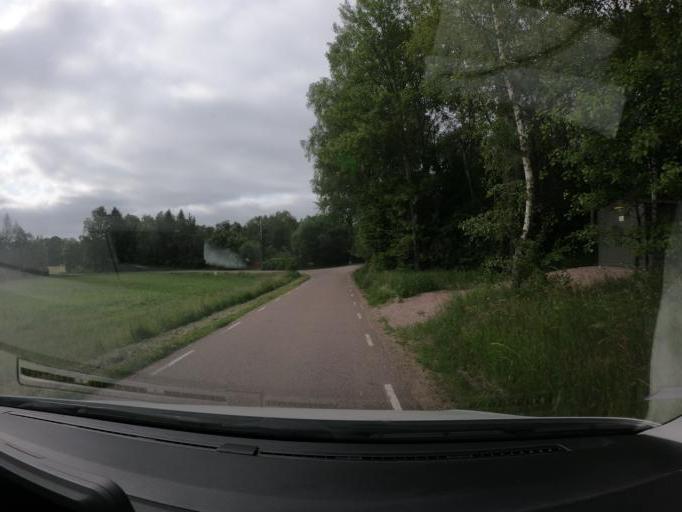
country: SE
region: Skane
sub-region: Klippans Kommun
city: Ljungbyhed
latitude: 56.0457
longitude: 13.3227
